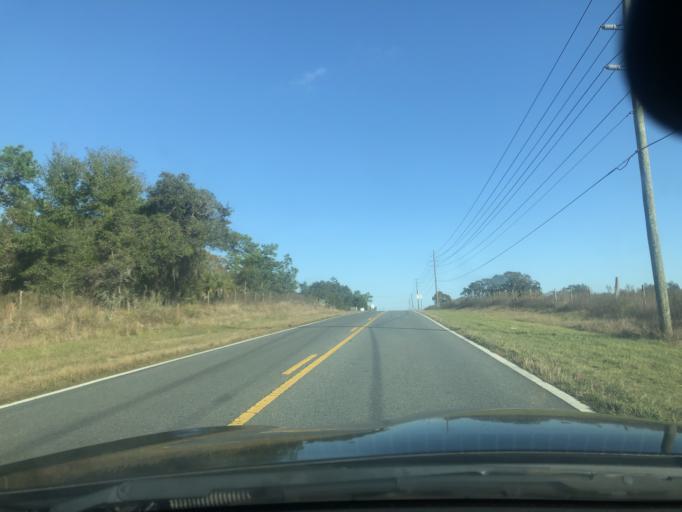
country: US
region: Florida
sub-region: Citrus County
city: Sugarmill Woods
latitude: 28.7640
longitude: -82.5234
